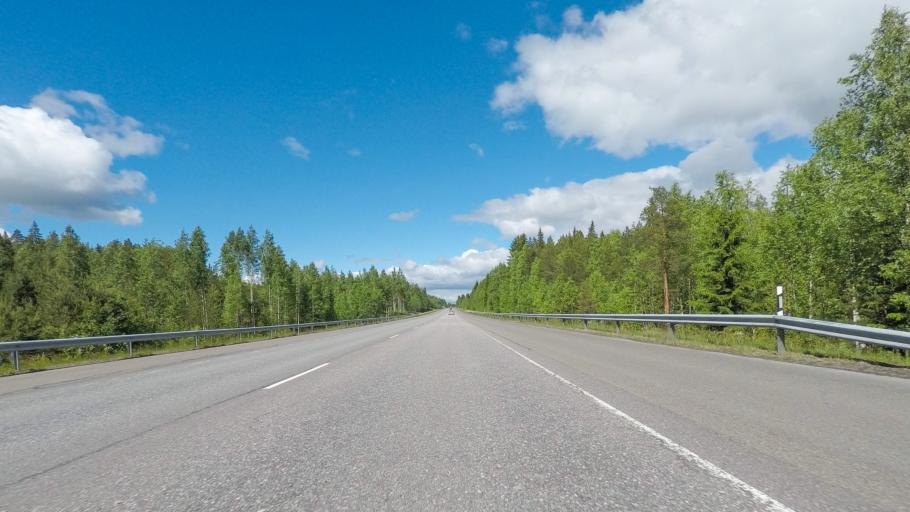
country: FI
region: Paijanne Tavastia
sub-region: Lahti
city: Heinola
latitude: 61.3197
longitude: 26.0427
